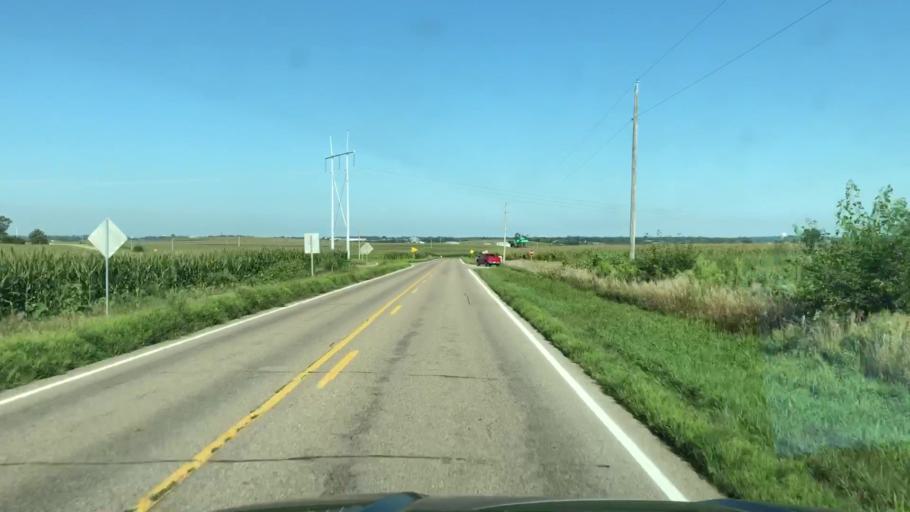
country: US
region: Iowa
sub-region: Woodbury County
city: Sergeant Bluff
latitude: 42.4305
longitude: -96.2850
